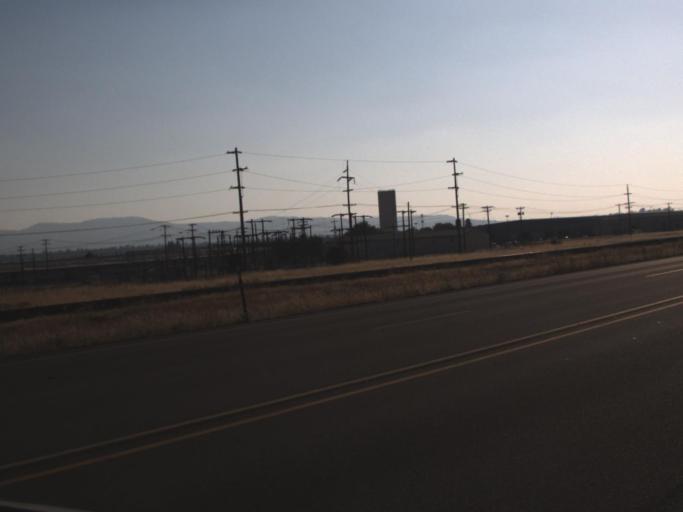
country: US
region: Washington
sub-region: Spokane County
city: Trentwood
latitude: 47.6962
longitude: -117.1856
